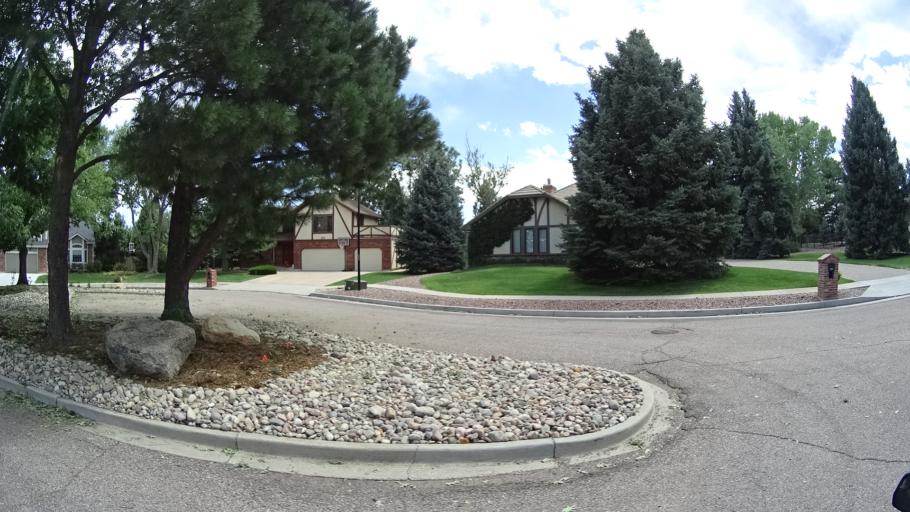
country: US
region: Colorado
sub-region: El Paso County
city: Stratmoor
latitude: 38.7862
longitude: -104.8251
